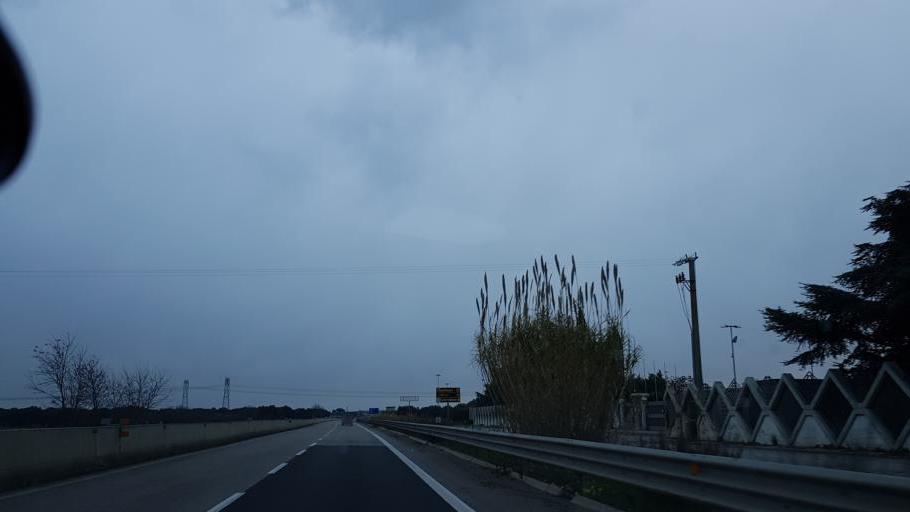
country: IT
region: Apulia
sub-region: Provincia di Brindisi
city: Mesagne
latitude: 40.5816
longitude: 17.8434
